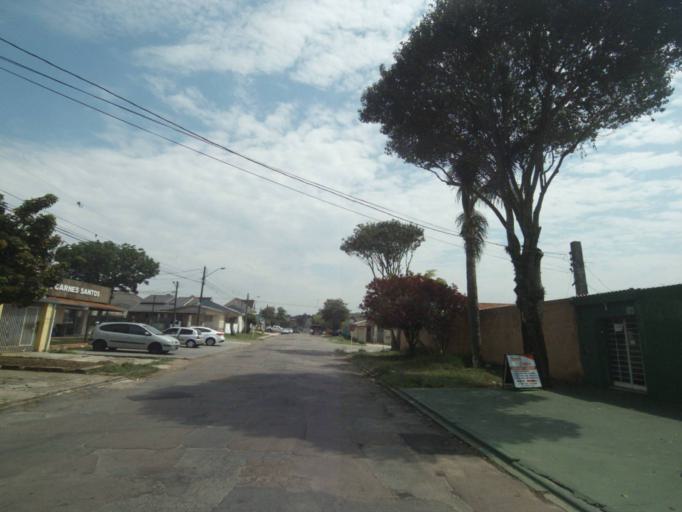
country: BR
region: Parana
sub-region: Pinhais
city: Pinhais
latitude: -25.4090
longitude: -49.2040
